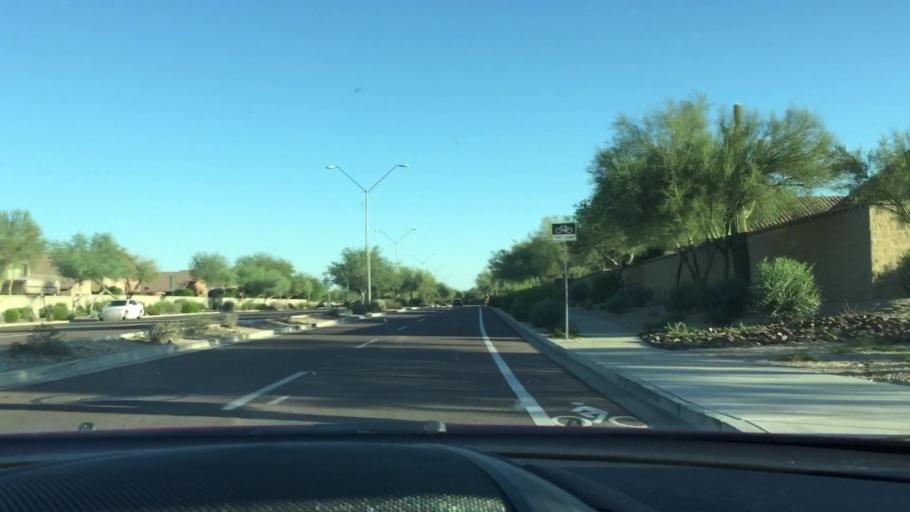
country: US
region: Arizona
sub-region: Maricopa County
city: Sun City West
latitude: 33.7273
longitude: -112.2430
